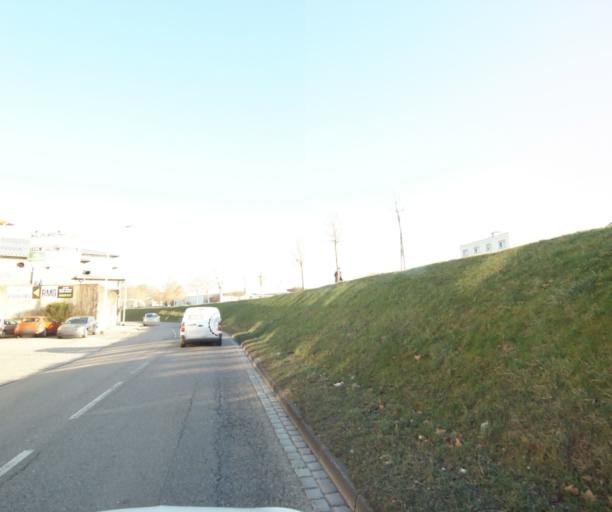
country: FR
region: Lorraine
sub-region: Departement de Meurthe-et-Moselle
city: Malzeville
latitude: 48.7027
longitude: 6.1831
